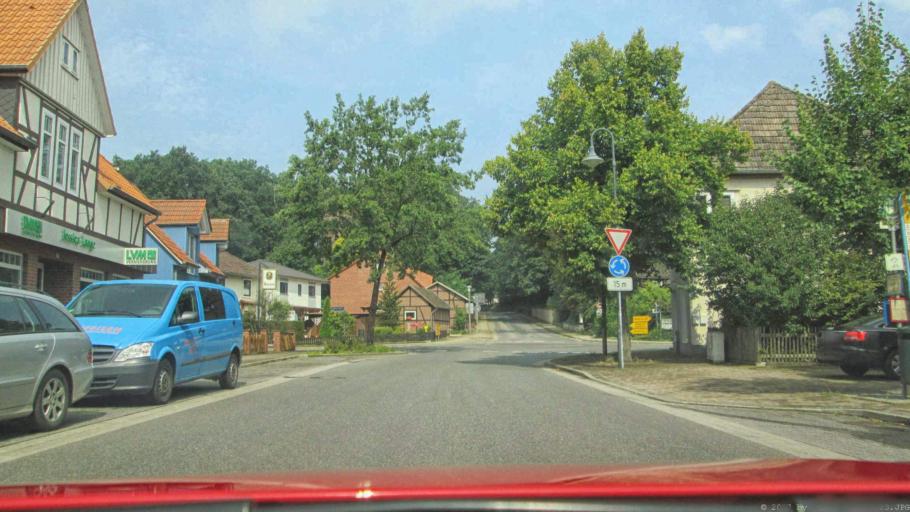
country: DE
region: Lower Saxony
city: Hankensbuttel
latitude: 52.7321
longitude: 10.6042
